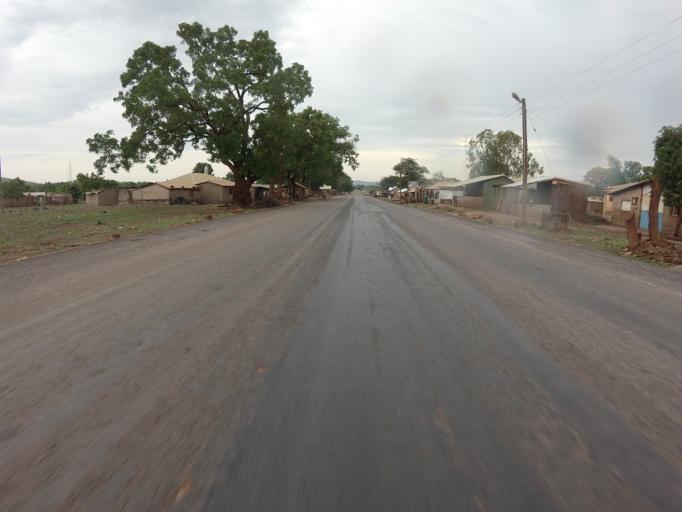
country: GH
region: Upper East
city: Bolgatanga
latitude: 10.8586
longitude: -0.6655
